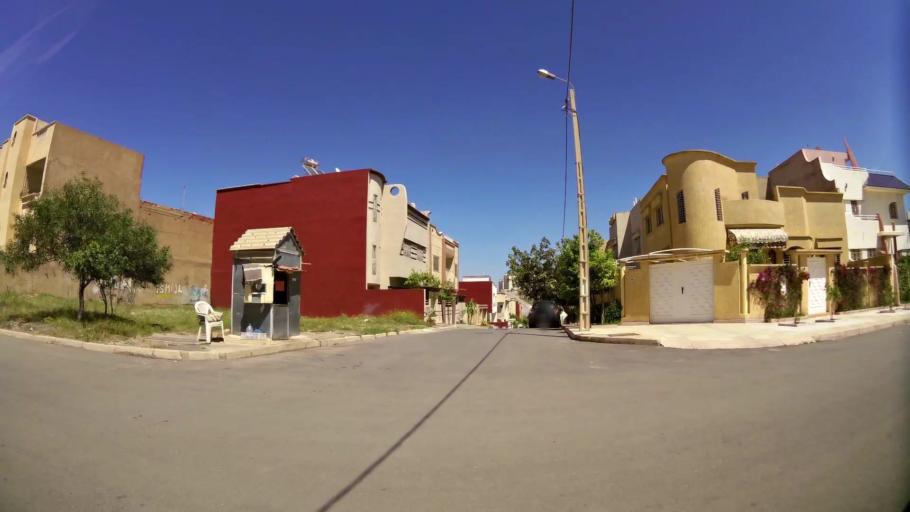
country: MA
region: Oriental
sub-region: Oujda-Angad
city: Oujda
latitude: 34.6520
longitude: -1.9152
